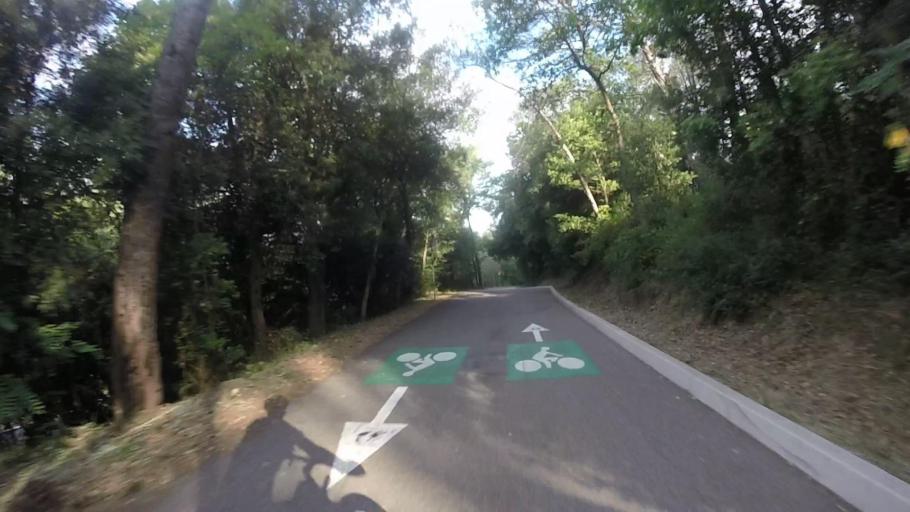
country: FR
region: Provence-Alpes-Cote d'Azur
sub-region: Departement des Alpes-Maritimes
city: Vallauris
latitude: 43.6141
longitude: 7.0447
